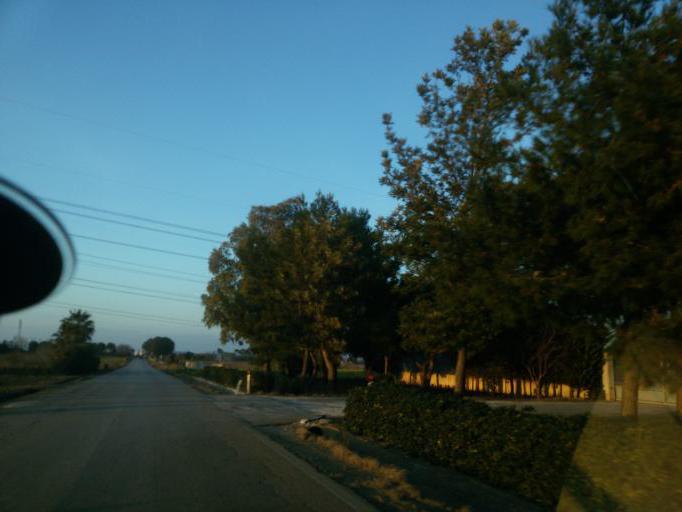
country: IT
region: Apulia
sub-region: Provincia di Brindisi
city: La Rosa
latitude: 40.6005
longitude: 17.9465
